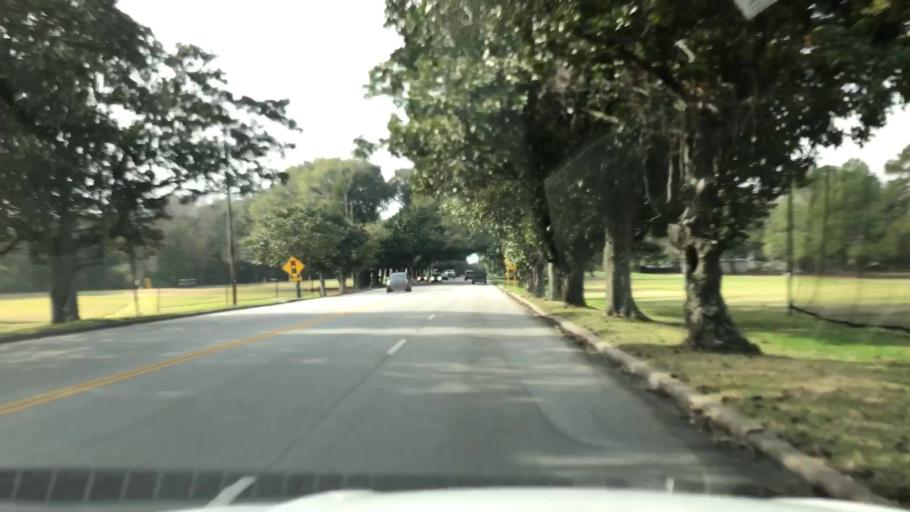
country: US
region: South Carolina
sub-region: Charleston County
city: Charleston
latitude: 32.7574
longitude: -79.9958
